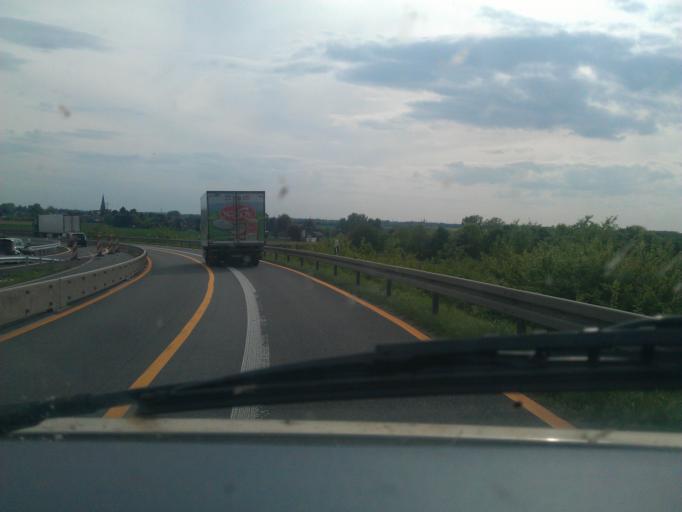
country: DE
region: North Rhine-Westphalia
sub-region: Regierungsbezirk Dusseldorf
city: Juchen
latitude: 51.1045
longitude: 6.4247
